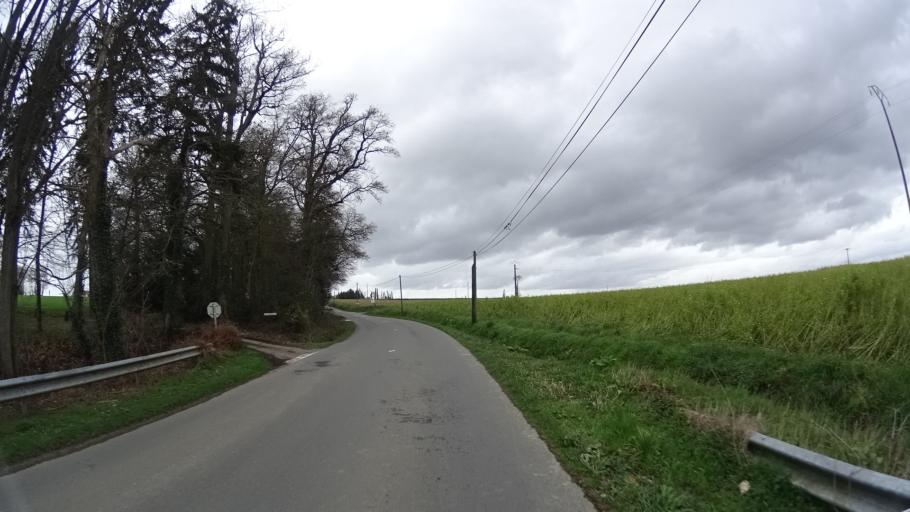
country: FR
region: Brittany
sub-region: Departement d'Ille-et-Vilaine
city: Saint-Gilles
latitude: 48.1806
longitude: -1.8314
